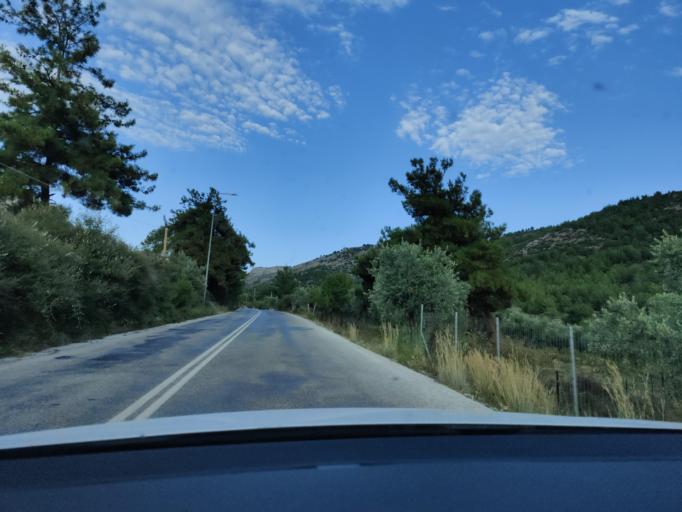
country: GR
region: East Macedonia and Thrace
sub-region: Nomos Kavalas
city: Limenaria
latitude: 40.6132
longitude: 24.6284
